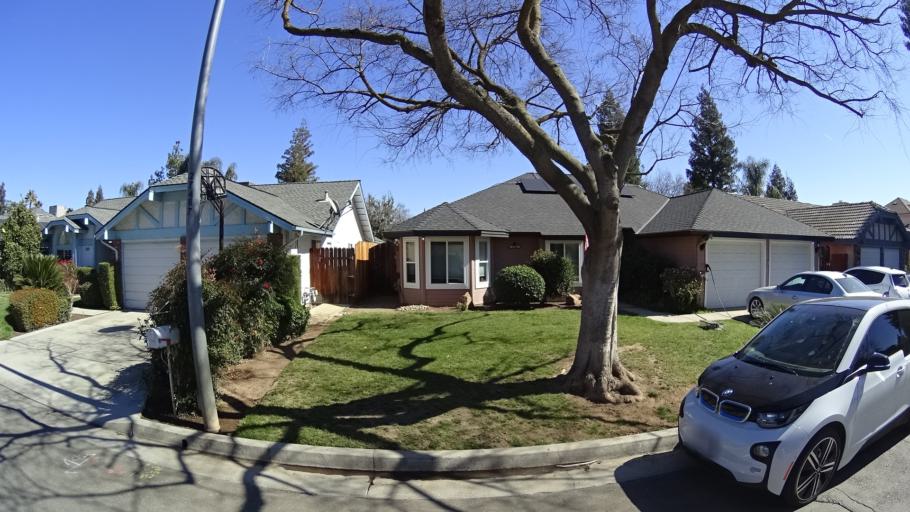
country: US
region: California
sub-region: Fresno County
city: Clovis
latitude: 36.8461
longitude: -119.7622
